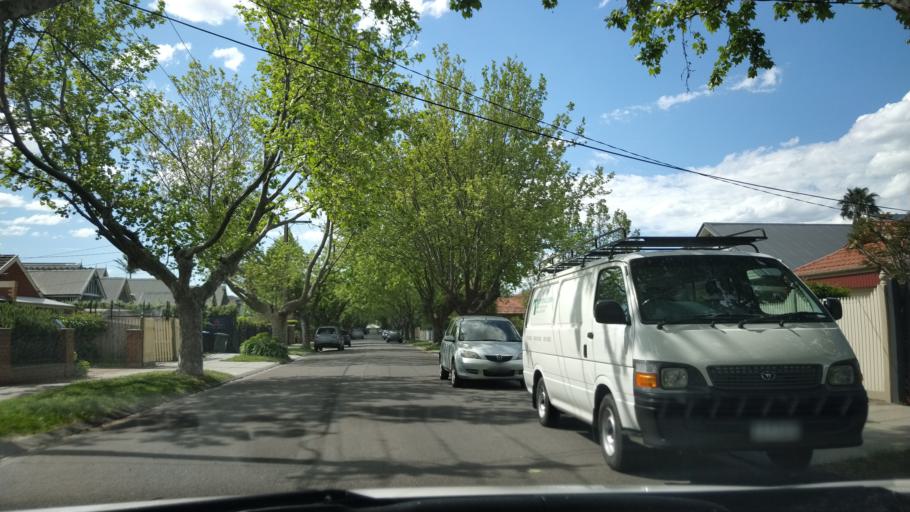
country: AU
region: Victoria
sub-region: Glen Eira
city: Carnegie
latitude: -37.8828
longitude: 145.0595
